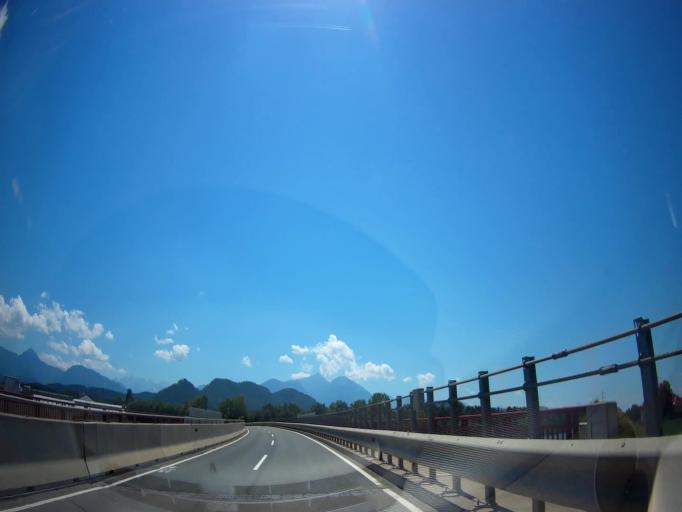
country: AT
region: Carinthia
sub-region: Politischer Bezirk Volkermarkt
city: Voelkermarkt
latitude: 46.6247
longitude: 14.6164
